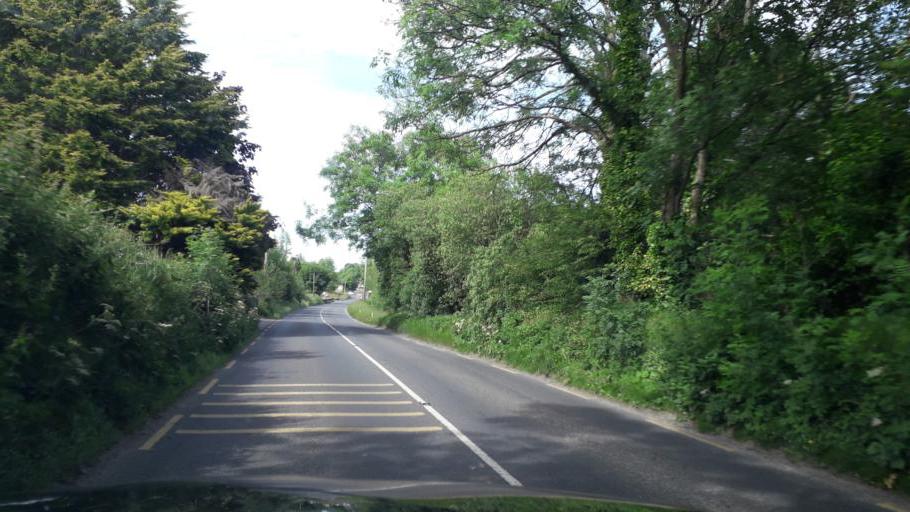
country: IE
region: Leinster
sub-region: Loch Garman
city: Castlebridge
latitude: 52.4131
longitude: -6.4220
